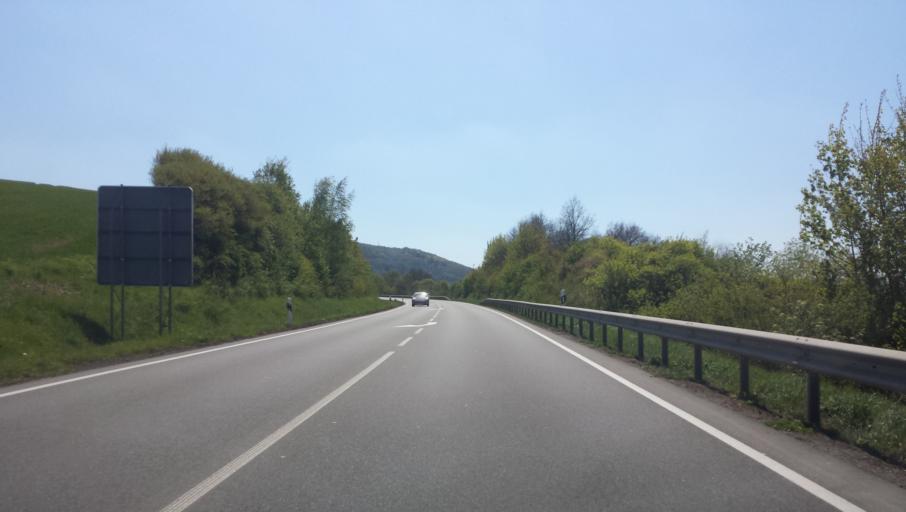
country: DE
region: Rheinland-Pfalz
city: Winnweiler
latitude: 49.5643
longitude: 7.8630
